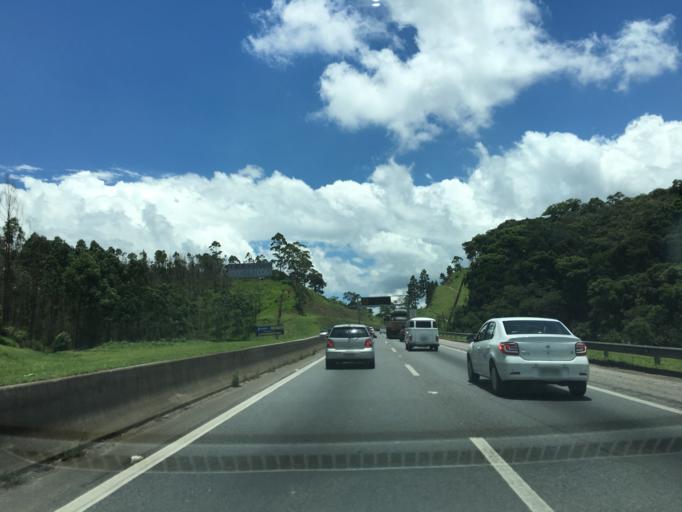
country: BR
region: Sao Paulo
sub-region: Mairipora
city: Mairipora
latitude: -23.2784
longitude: -46.5861
